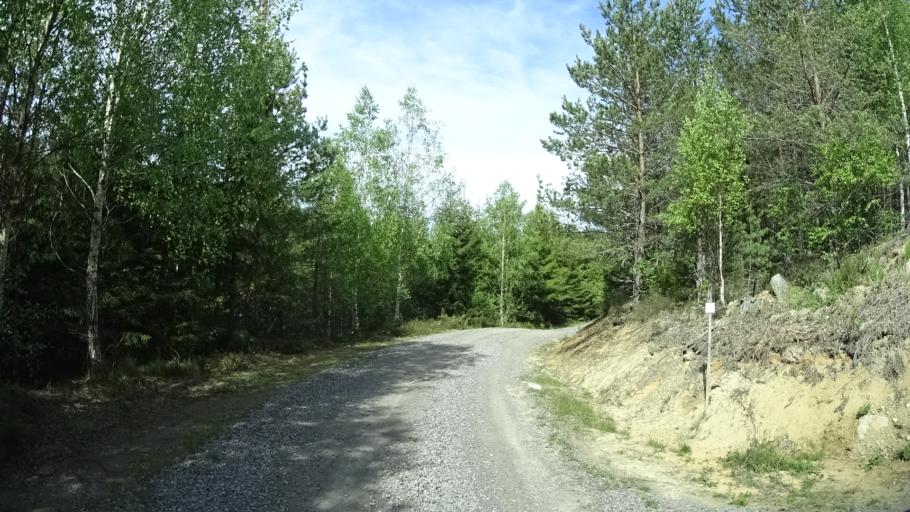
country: SE
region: OEstergoetland
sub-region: Finspangs Kommun
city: Finspang
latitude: 58.7946
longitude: 15.8557
